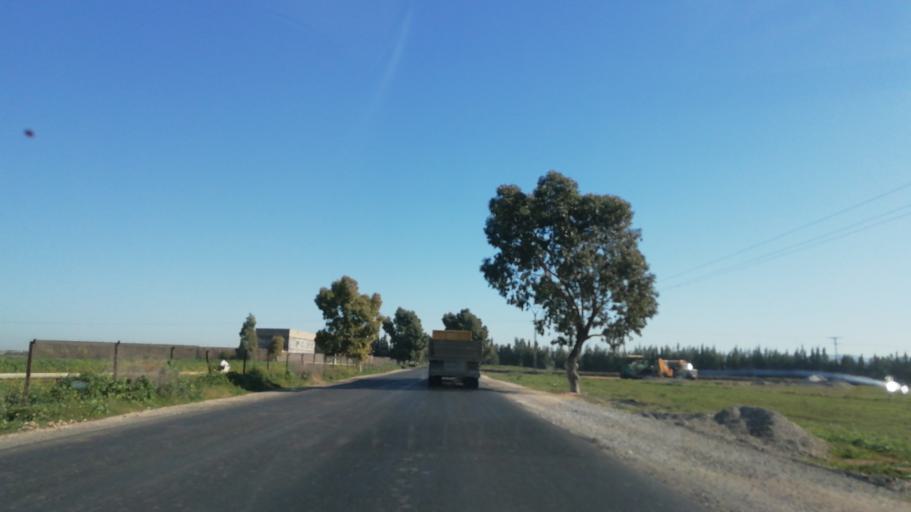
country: DZ
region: Relizane
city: Zemoura
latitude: 35.7586
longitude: 0.6651
